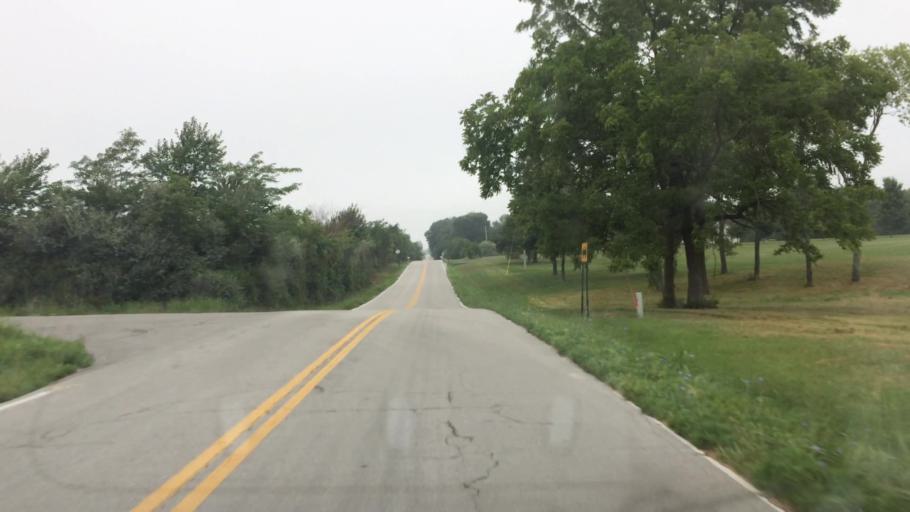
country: US
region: Missouri
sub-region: Greene County
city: Strafford
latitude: 37.2720
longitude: -93.1872
